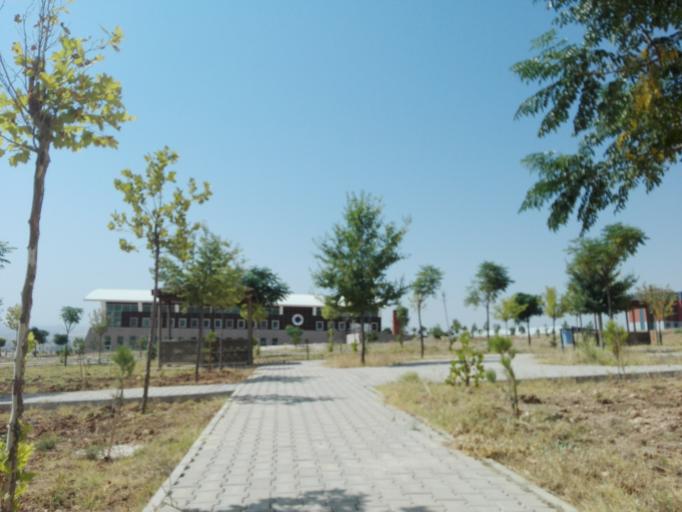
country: TR
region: Batman
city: Oymatas
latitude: 37.7914
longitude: 41.0654
